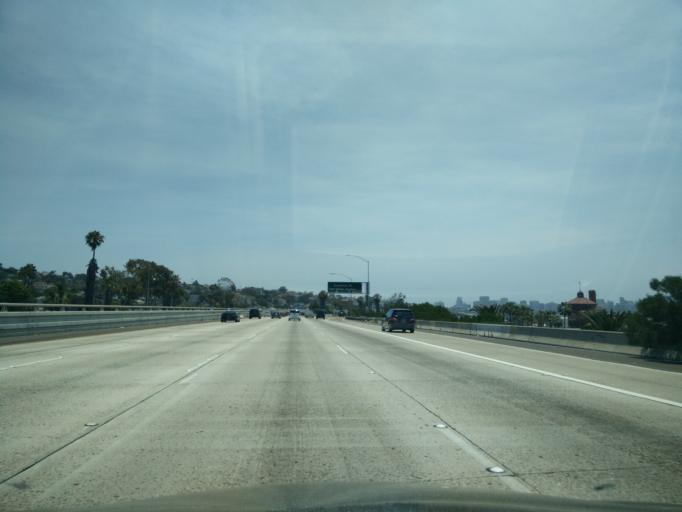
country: US
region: California
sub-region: San Diego County
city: San Diego
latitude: 32.7437
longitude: -117.1854
